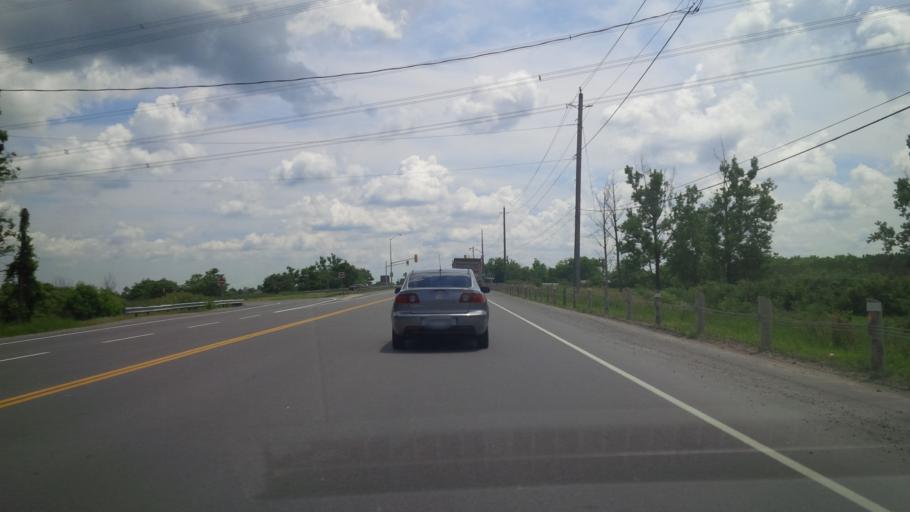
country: CA
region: Ontario
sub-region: Wellington County
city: Guelph
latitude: 43.4551
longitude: -80.1273
